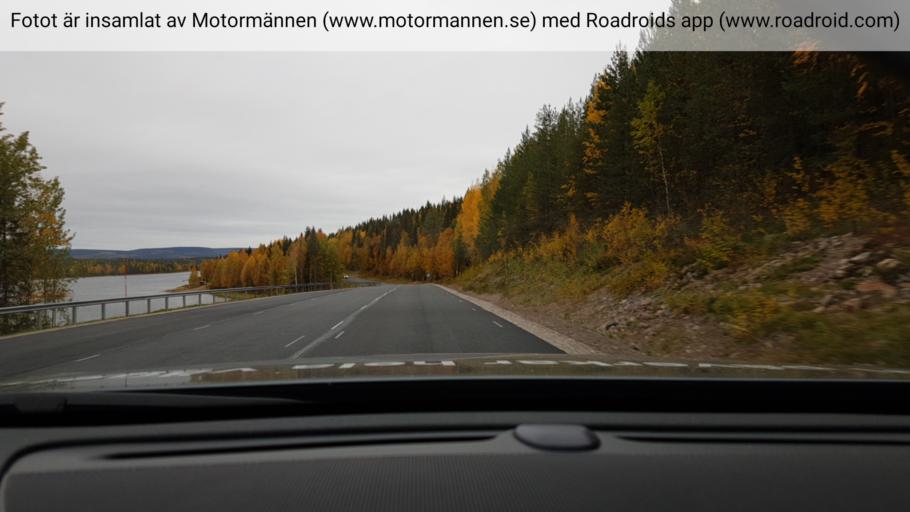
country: SE
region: Norrbotten
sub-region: Overkalix Kommun
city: OEverkalix
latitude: 66.4823
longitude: 22.7854
